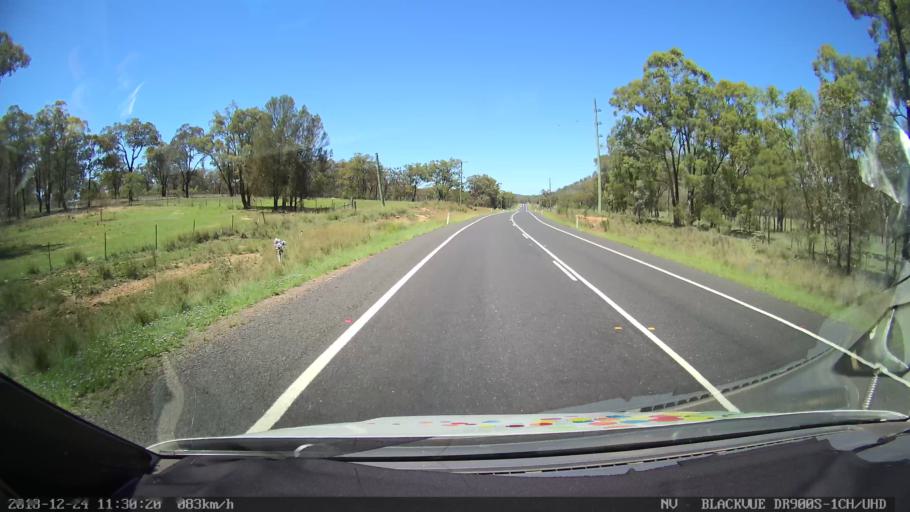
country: AU
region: New South Wales
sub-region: Upper Hunter Shire
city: Merriwa
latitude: -32.2035
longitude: 150.4672
